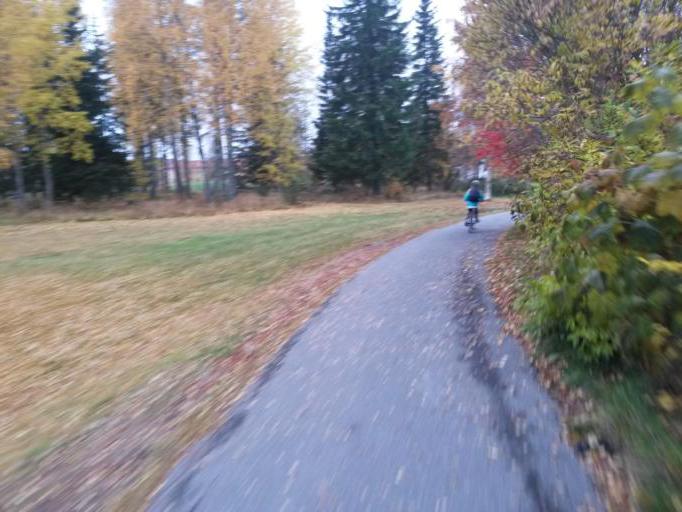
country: SE
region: Vaesterbotten
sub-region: Skelleftea Kommun
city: Soedra Bergsbyn
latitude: 64.7550
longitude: 21.0324
